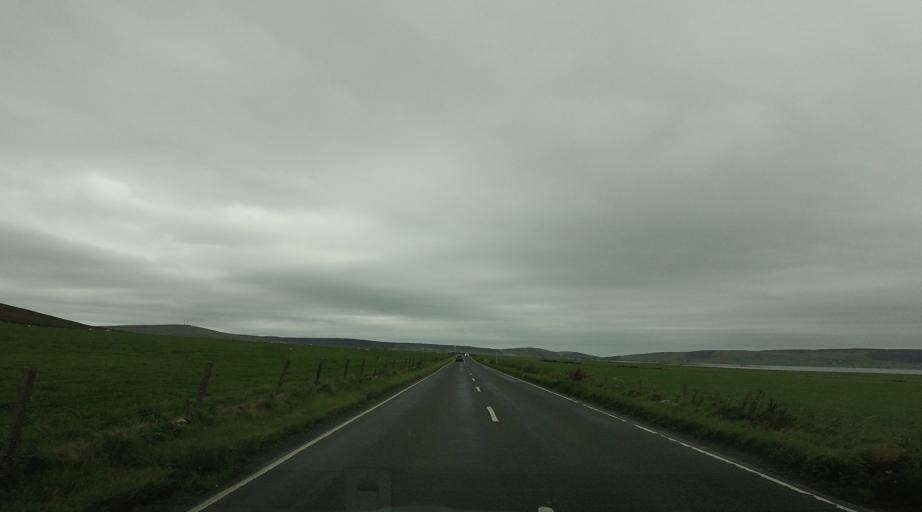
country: GB
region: Scotland
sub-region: Orkney Islands
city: Orkney
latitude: 59.0020
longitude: -3.0179
